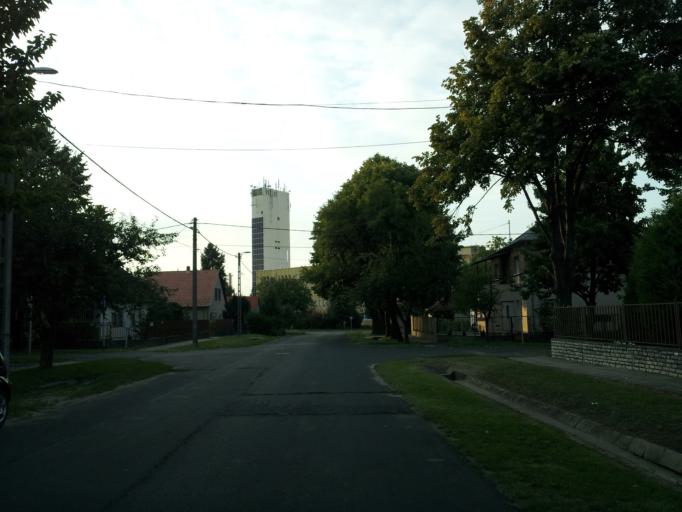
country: HU
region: Somogy
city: Siofok
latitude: 46.8990
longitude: 18.0442
